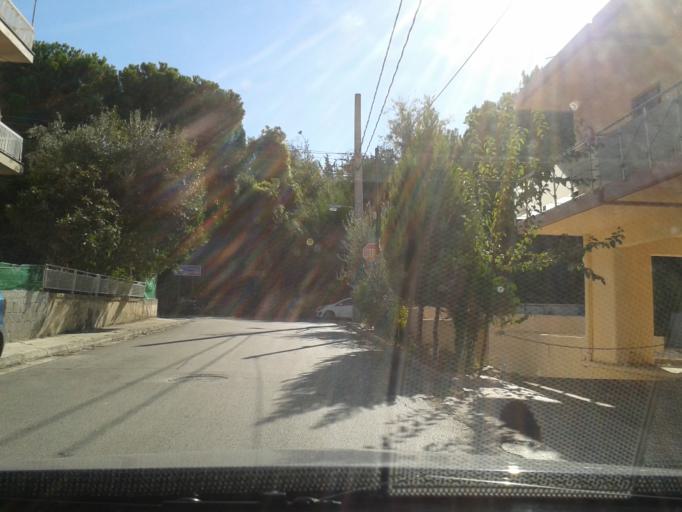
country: GR
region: Attica
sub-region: Nomarchia Athinas
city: Chaidari
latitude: 38.0106
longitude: 23.6457
